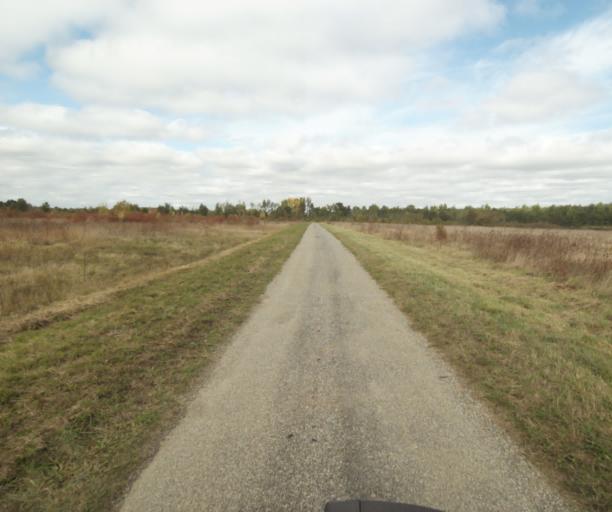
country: FR
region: Midi-Pyrenees
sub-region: Departement du Tarn-et-Garonne
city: Finhan
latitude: 43.9237
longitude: 1.2084
